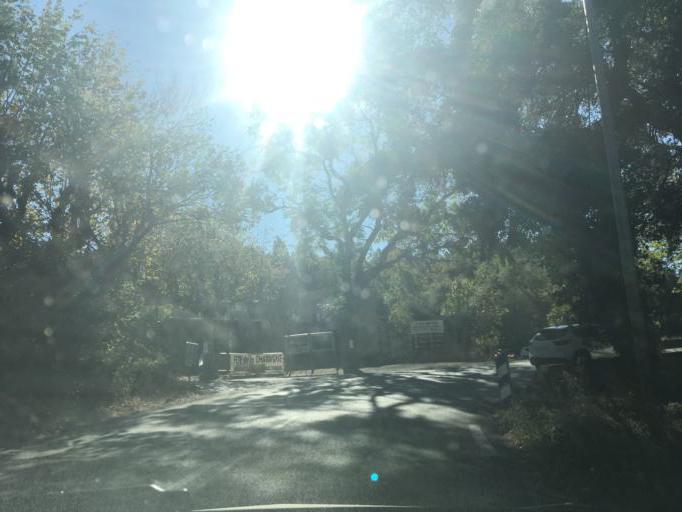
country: FR
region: Provence-Alpes-Cote d'Azur
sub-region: Departement du Var
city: La Garde-Freinet
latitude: 43.3172
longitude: 6.4723
